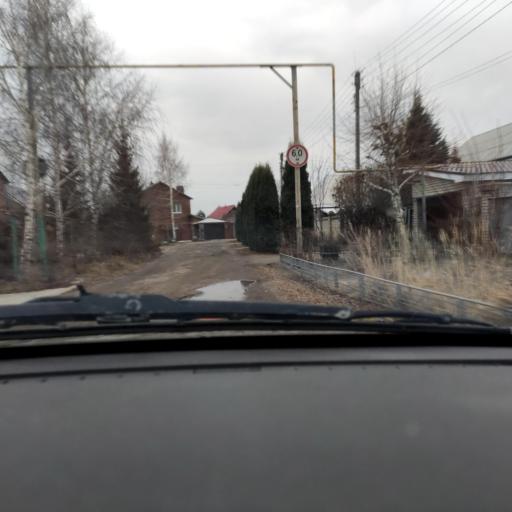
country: RU
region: Samara
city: Podstepki
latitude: 53.5171
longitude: 49.1863
